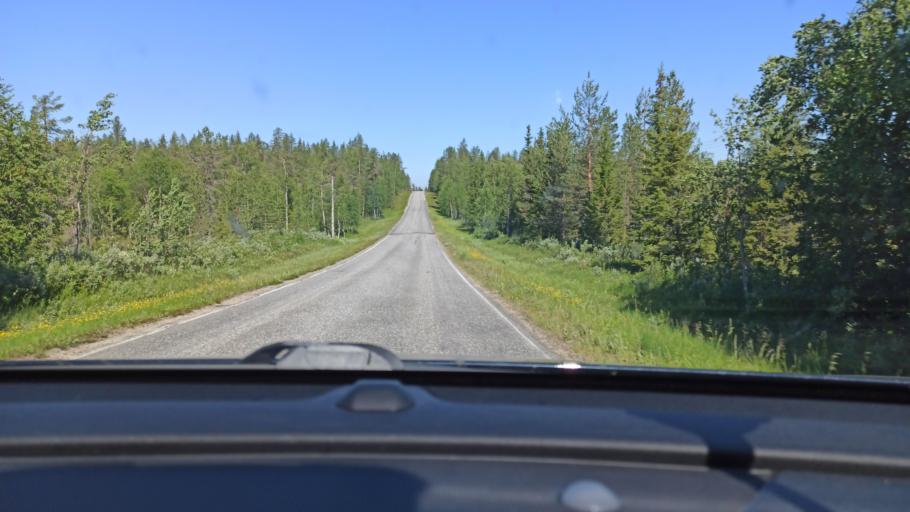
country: FI
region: Lapland
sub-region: Tunturi-Lappi
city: Kolari
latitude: 67.6773
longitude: 24.1422
